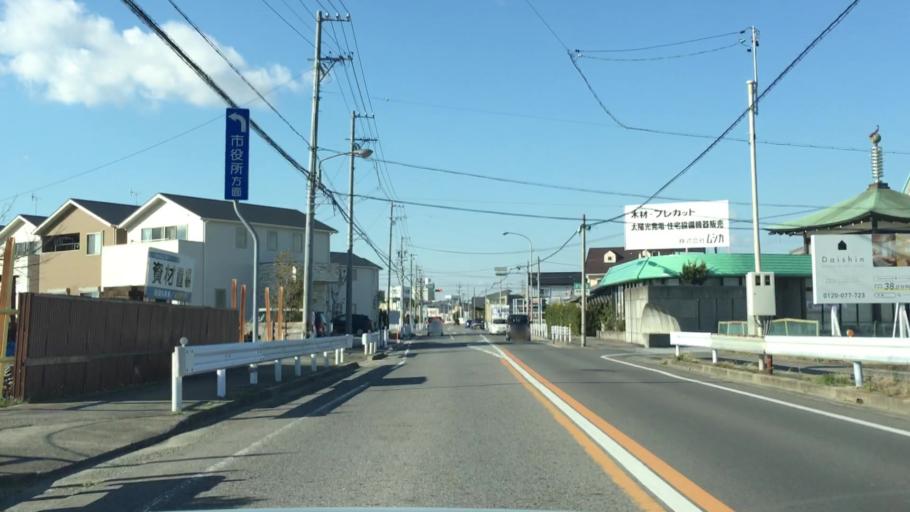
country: JP
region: Aichi
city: Nishio
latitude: 34.8518
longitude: 137.0592
